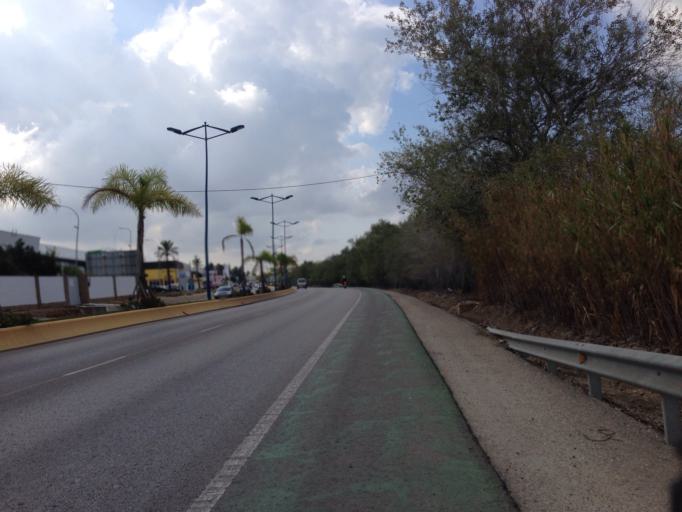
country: ES
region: Andalusia
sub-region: Provincia de Cadiz
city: Chiclana de la Frontera
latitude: 36.4389
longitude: -6.1443
